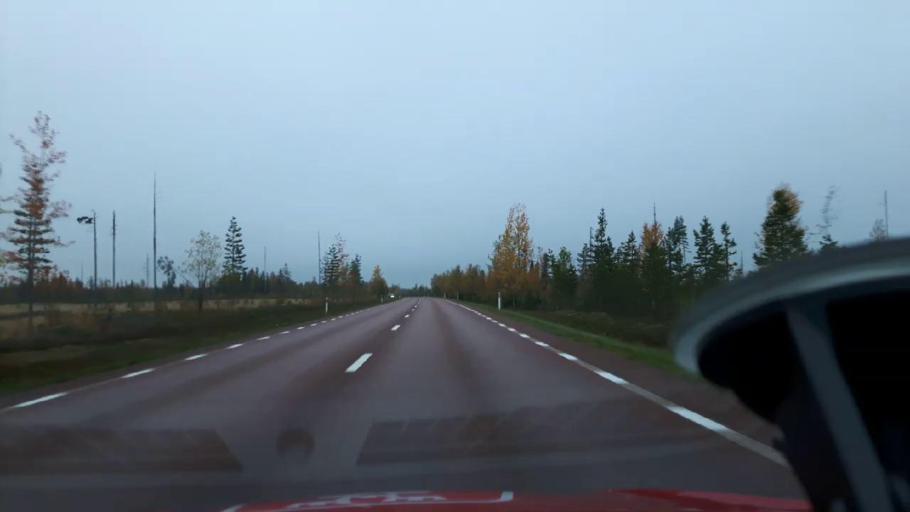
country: SE
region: Jaemtland
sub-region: Bergs Kommun
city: Hoverberg
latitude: 62.5304
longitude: 14.4469
